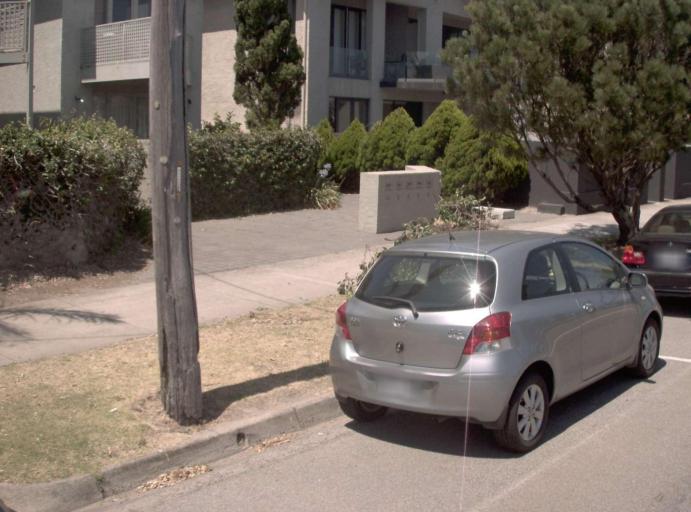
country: AU
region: Victoria
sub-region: Port Phillip
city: Saint Kilda
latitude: -37.8733
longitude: 144.9767
